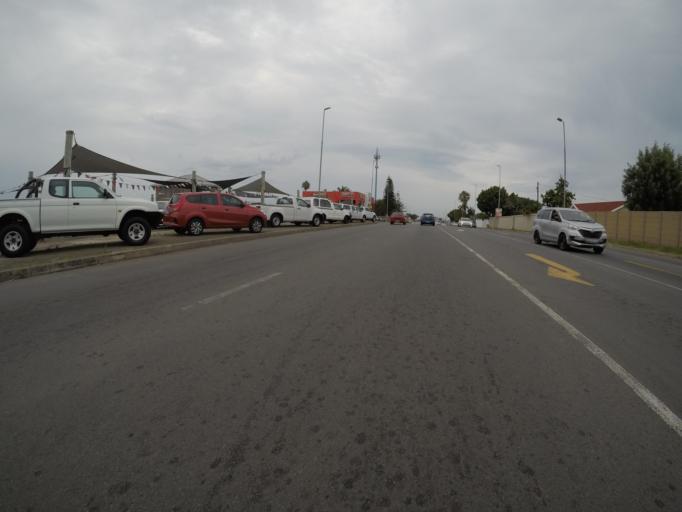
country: ZA
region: Eastern Cape
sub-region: Buffalo City Metropolitan Municipality
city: East London
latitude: -32.9913
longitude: 27.8631
